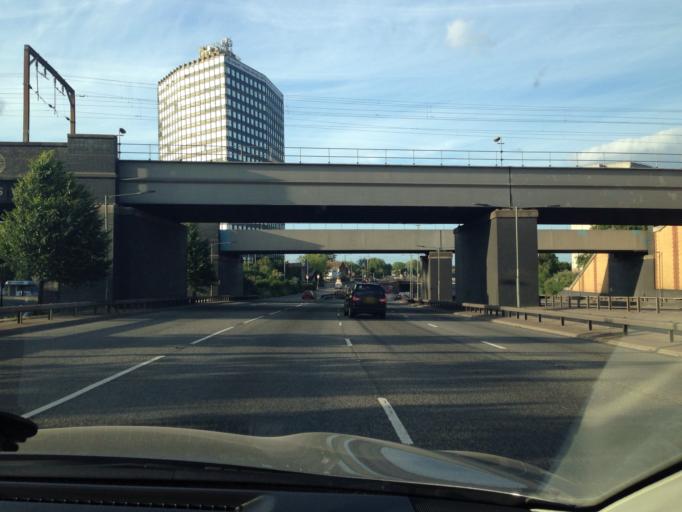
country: GB
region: England
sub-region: Greater London
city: Wembley
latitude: 51.5428
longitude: -0.2753
